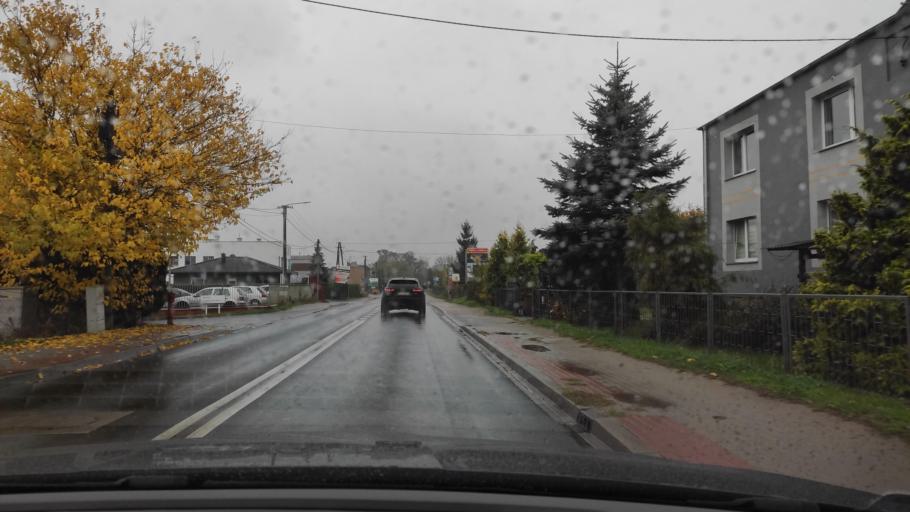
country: PL
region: Greater Poland Voivodeship
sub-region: Powiat poznanski
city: Swarzedz
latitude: 52.3845
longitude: 17.0740
